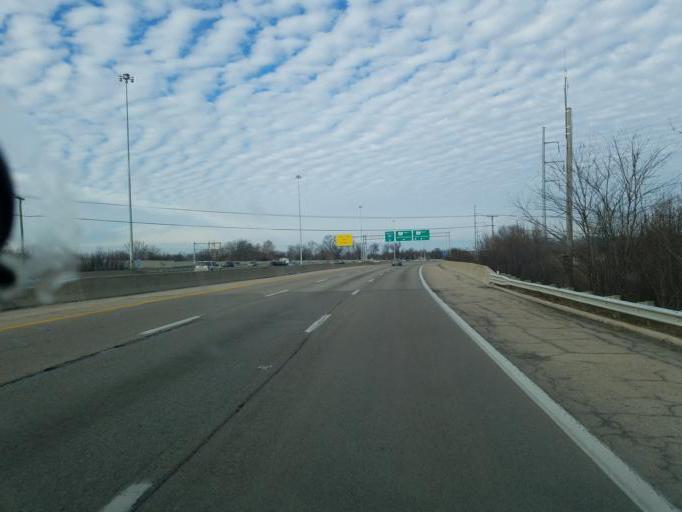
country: US
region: Ohio
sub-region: Franklin County
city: Huber Ridge
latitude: 40.0691
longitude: -82.9069
